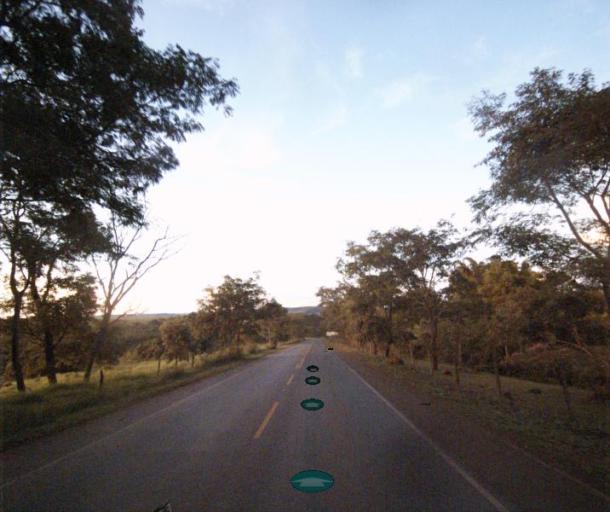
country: BR
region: Goias
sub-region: Pirenopolis
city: Pirenopolis
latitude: -15.9962
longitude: -48.8384
